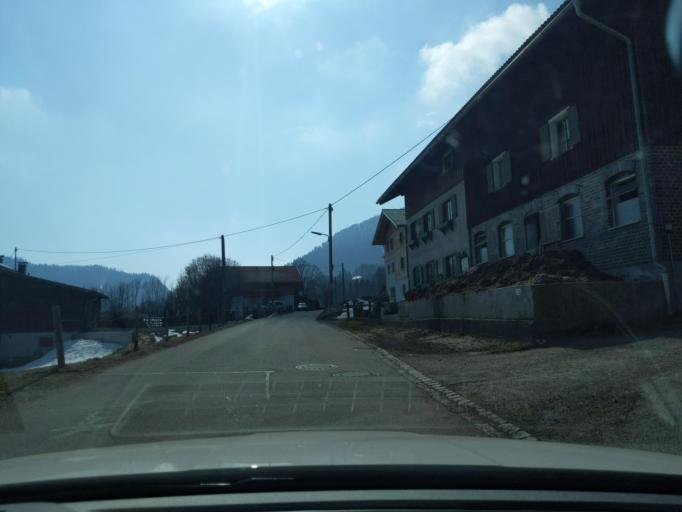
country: DE
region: Bavaria
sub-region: Swabia
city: Obermaiselstein
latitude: 47.4532
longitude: 10.2334
